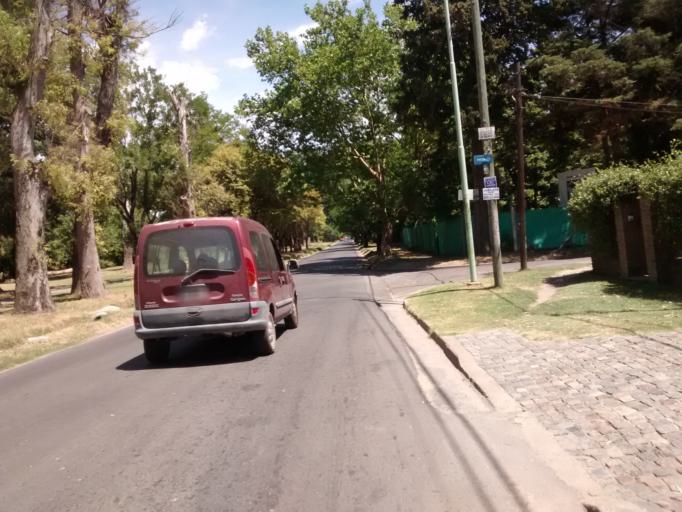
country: AR
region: Buenos Aires
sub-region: Partido de La Plata
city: La Plata
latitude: -34.8781
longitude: -58.0135
